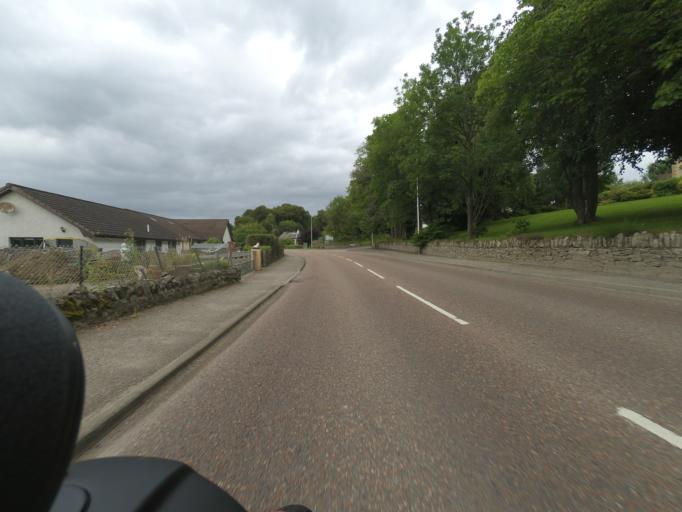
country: GB
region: Scotland
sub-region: Highland
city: Muir of Ord
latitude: 57.5681
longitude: -4.5791
